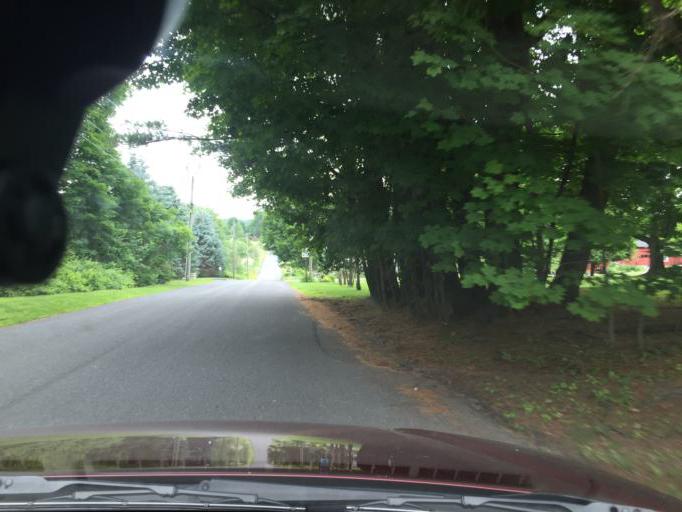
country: US
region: Connecticut
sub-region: Litchfield County
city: Litchfield
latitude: 41.7084
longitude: -73.2356
